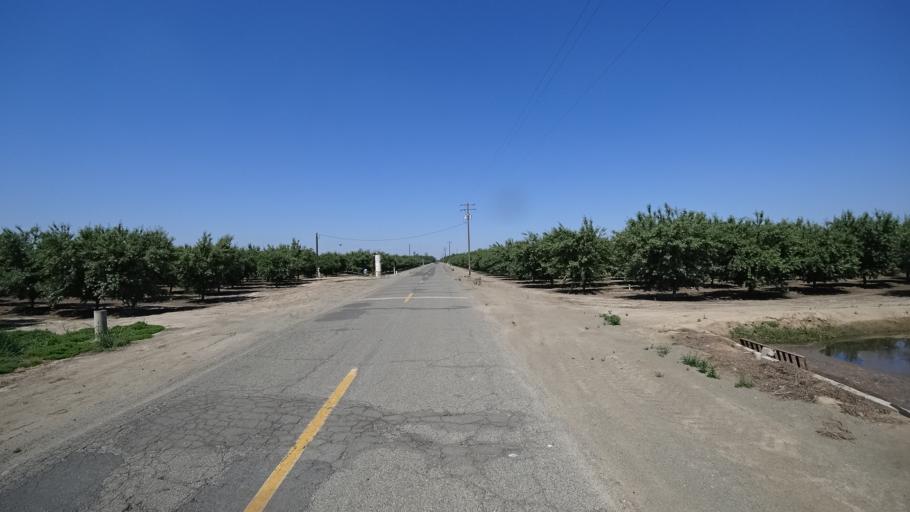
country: US
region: California
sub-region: Fresno County
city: Kingsburg
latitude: 36.4452
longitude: -119.5844
